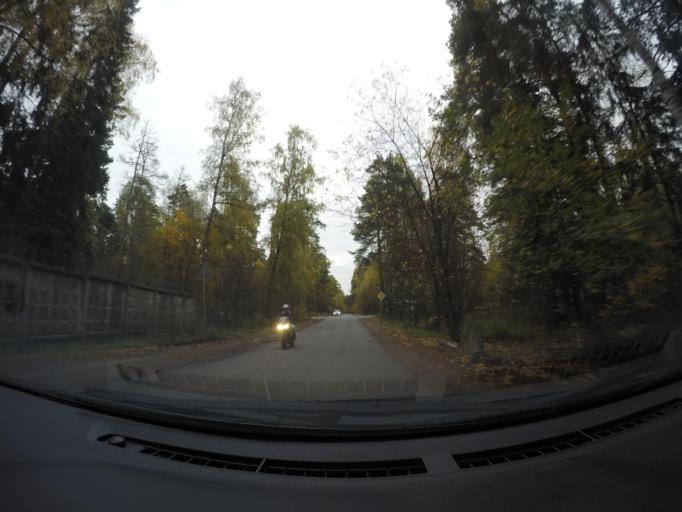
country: RU
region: Moskovskaya
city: Vishnyakovskiye Dachi
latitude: 55.8066
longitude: 38.1125
